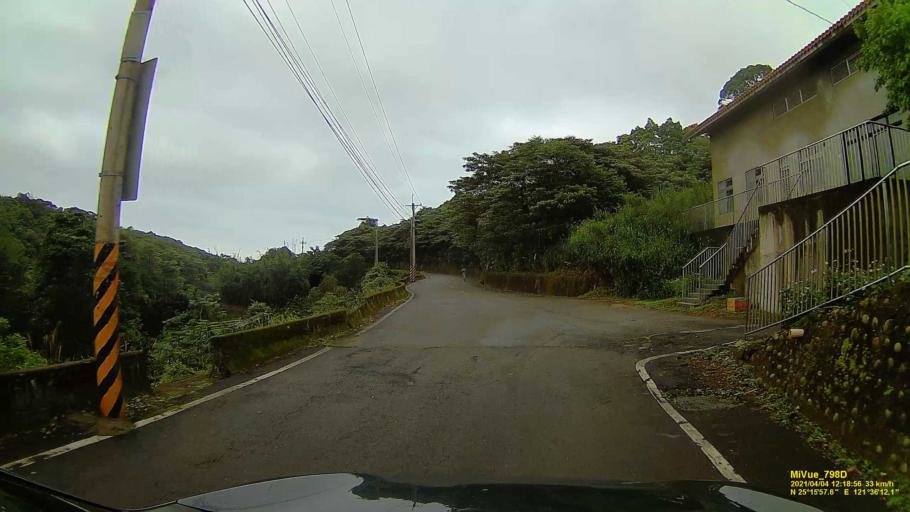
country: TW
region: Taiwan
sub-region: Keelung
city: Keelung
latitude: 25.2661
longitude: 121.6034
